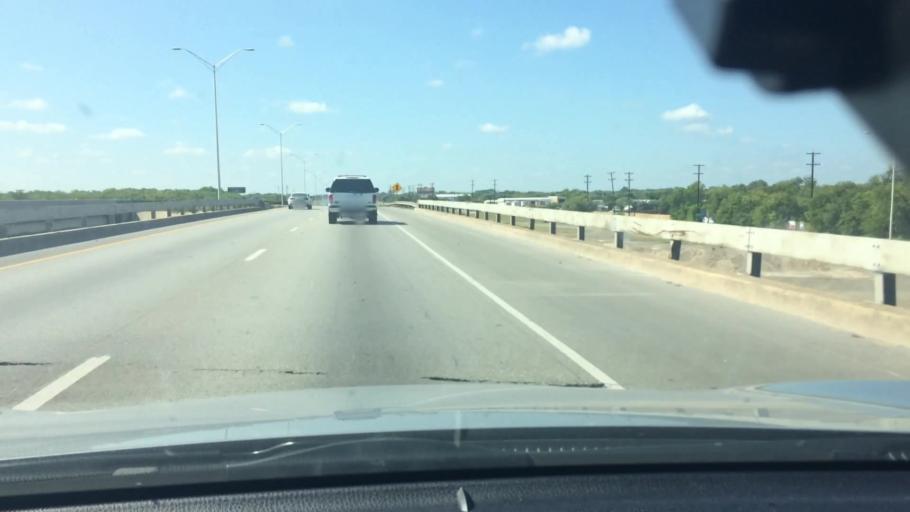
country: US
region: Texas
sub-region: Bexar County
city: Kirby
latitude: 29.4237
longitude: -98.3894
